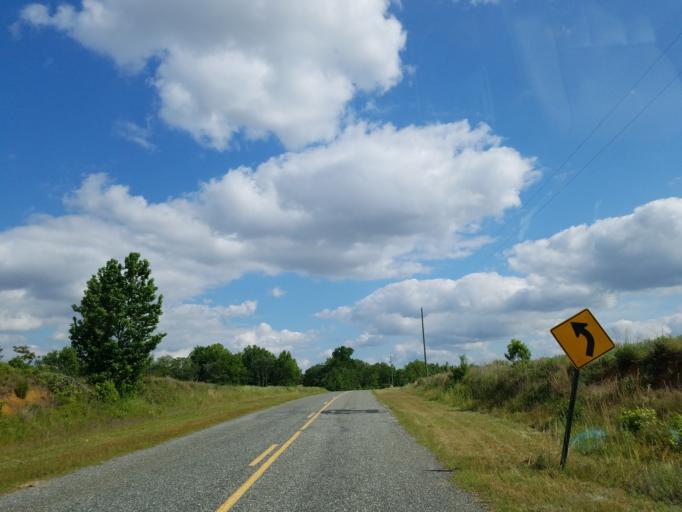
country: US
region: Georgia
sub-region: Dooly County
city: Unadilla
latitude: 32.2480
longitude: -83.7812
